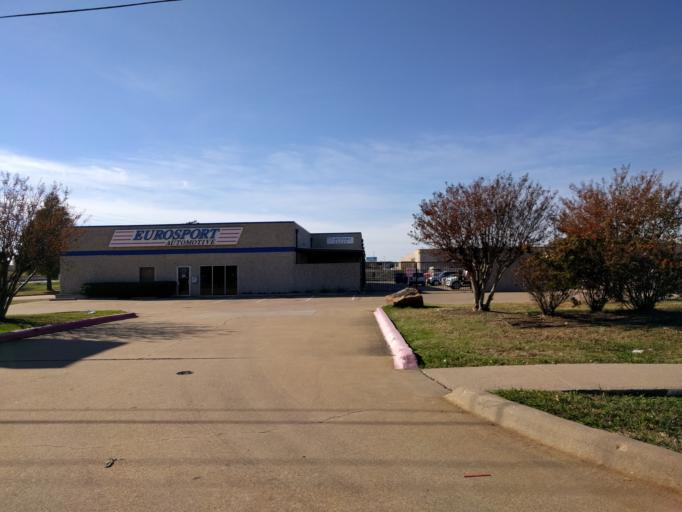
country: US
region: Texas
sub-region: Dallas County
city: Richardson
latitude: 33.0010
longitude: -96.7680
